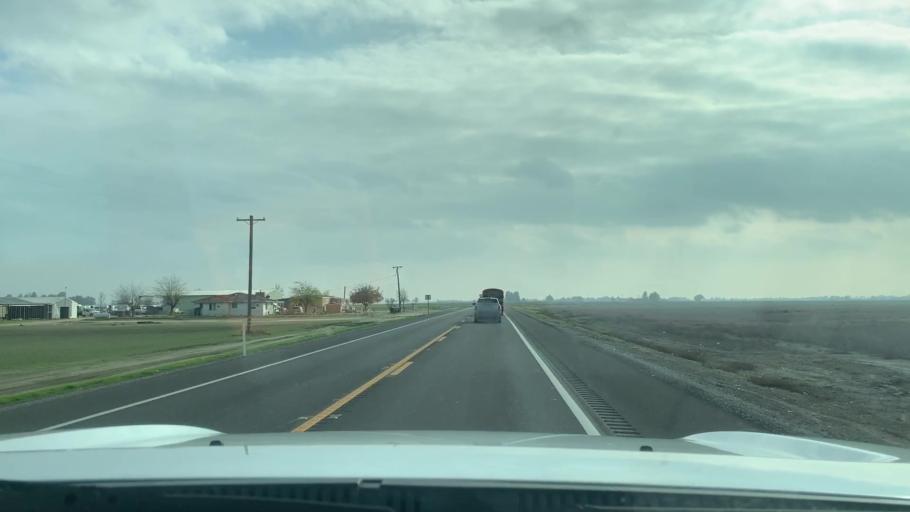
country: US
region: California
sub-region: Kings County
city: Stratford
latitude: 36.2256
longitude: -119.8164
